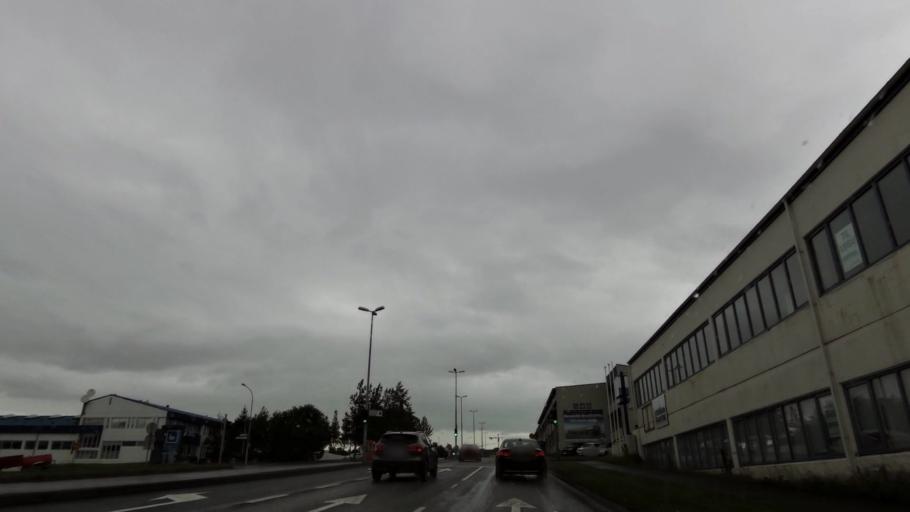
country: IS
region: Capital Region
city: Reykjavik
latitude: 64.1279
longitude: -21.8123
